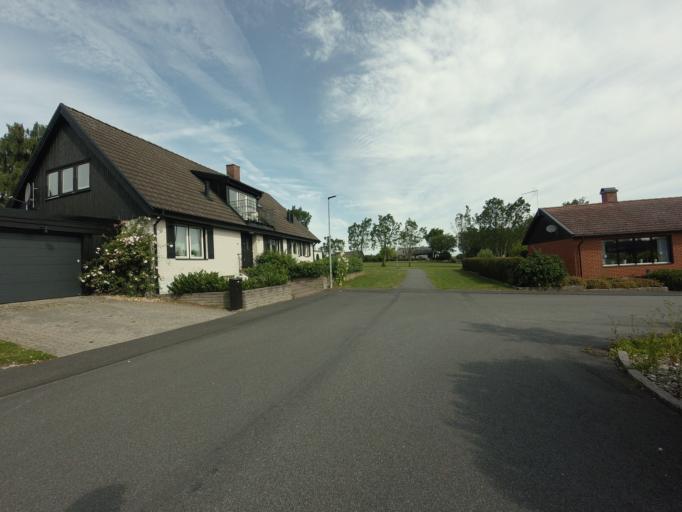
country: SE
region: Skane
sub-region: Simrishamns Kommun
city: Simrishamn
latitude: 55.5424
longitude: 14.3497
